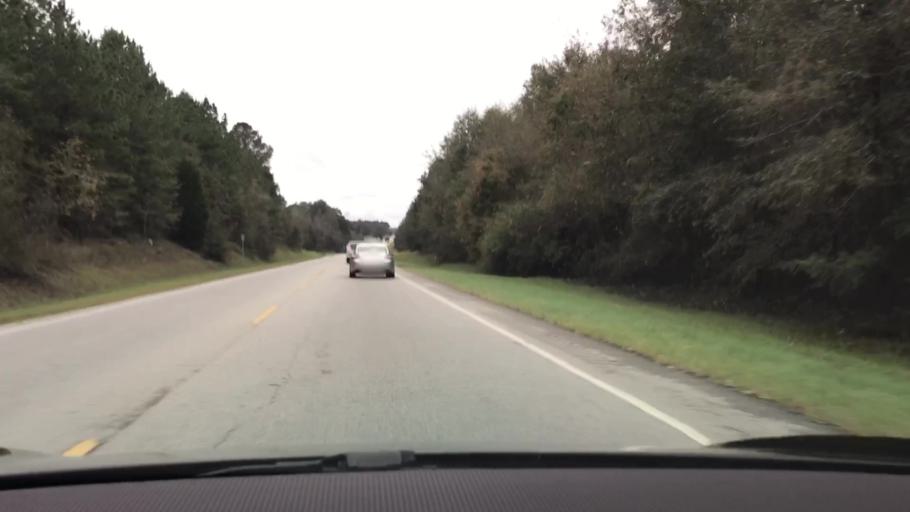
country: US
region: Georgia
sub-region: Jefferson County
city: Wadley
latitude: 32.8998
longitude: -82.4002
